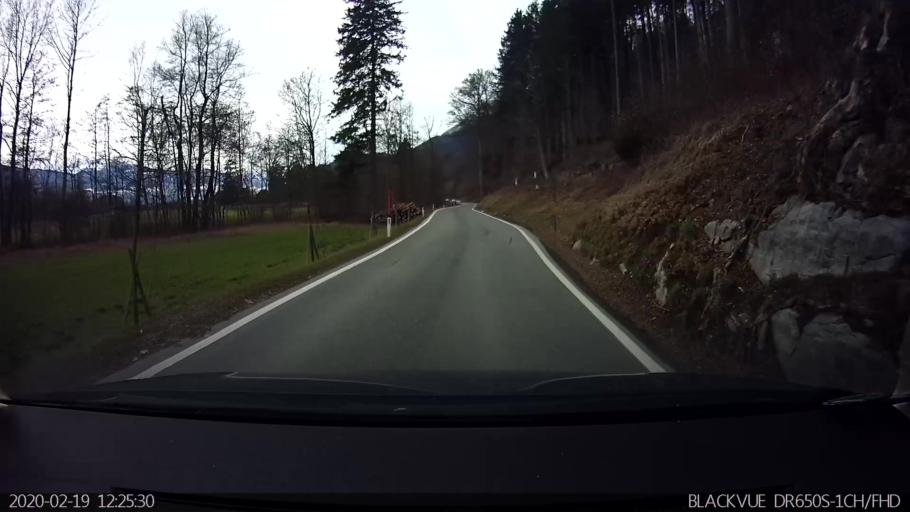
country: AT
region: Tyrol
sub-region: Politischer Bezirk Schwaz
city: Buch bei Jenbach
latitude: 47.3801
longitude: 11.7345
